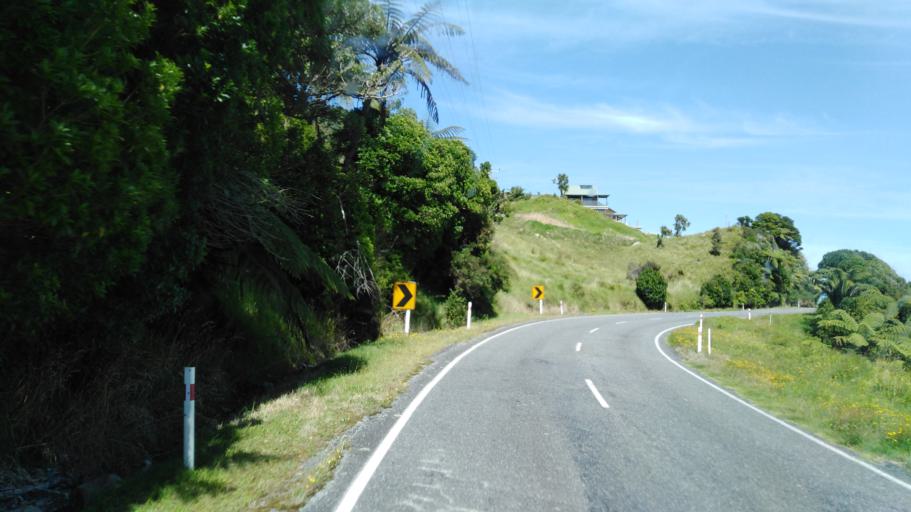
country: NZ
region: West Coast
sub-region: Buller District
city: Westport
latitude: -41.5721
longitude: 171.9055
